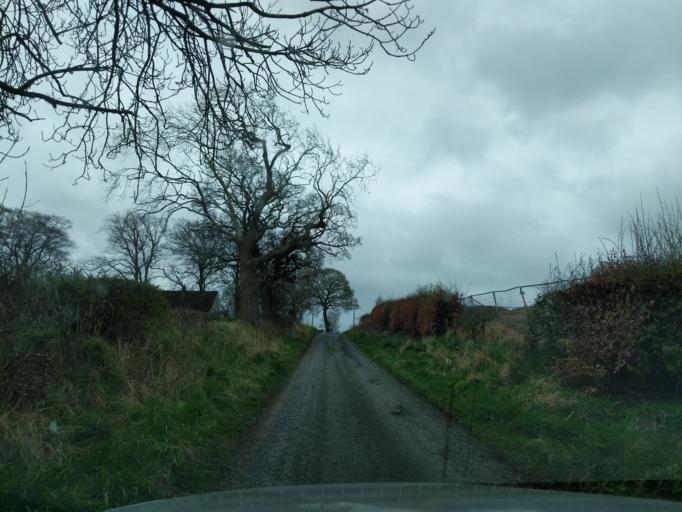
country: GB
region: Scotland
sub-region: Edinburgh
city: Balerno
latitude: 55.8937
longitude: -3.3376
